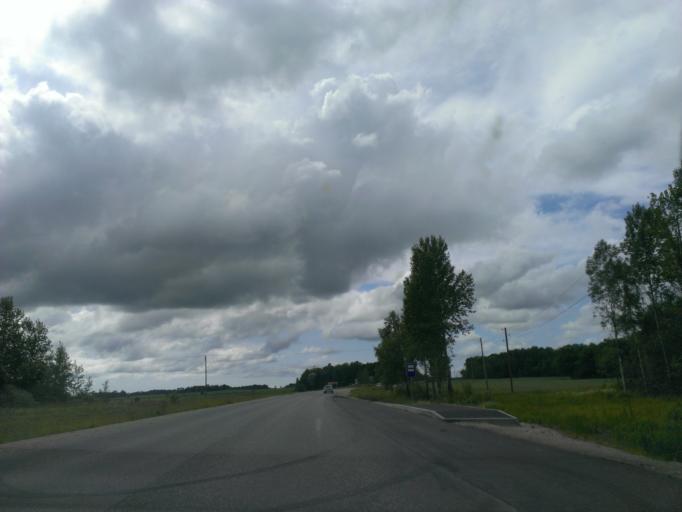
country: LV
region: Durbe
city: Liegi
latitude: 56.5882
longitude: 21.4376
